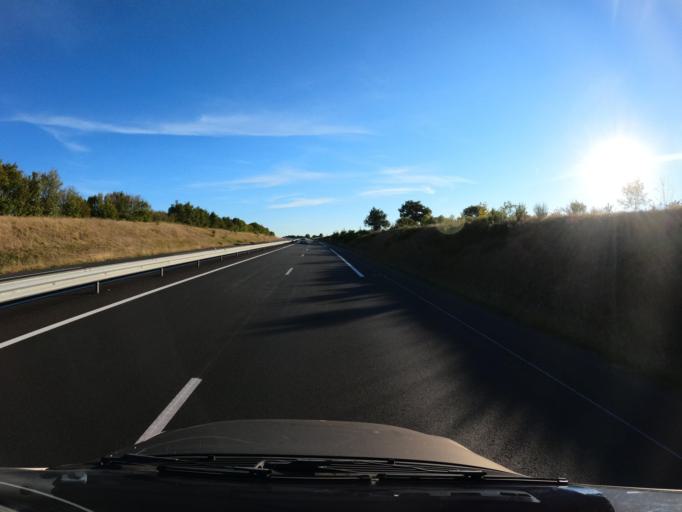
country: FR
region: Pays de la Loire
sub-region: Departement de la Vendee
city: Mortagne-sur-Sevre
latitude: 46.9856
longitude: -0.9174
